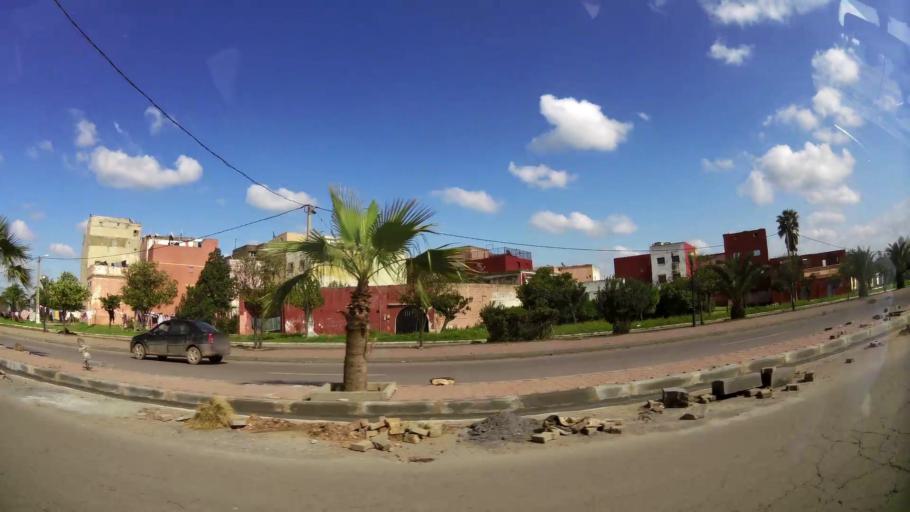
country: MA
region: Grand Casablanca
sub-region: Mediouna
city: Mediouna
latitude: 33.4571
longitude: -7.5209
